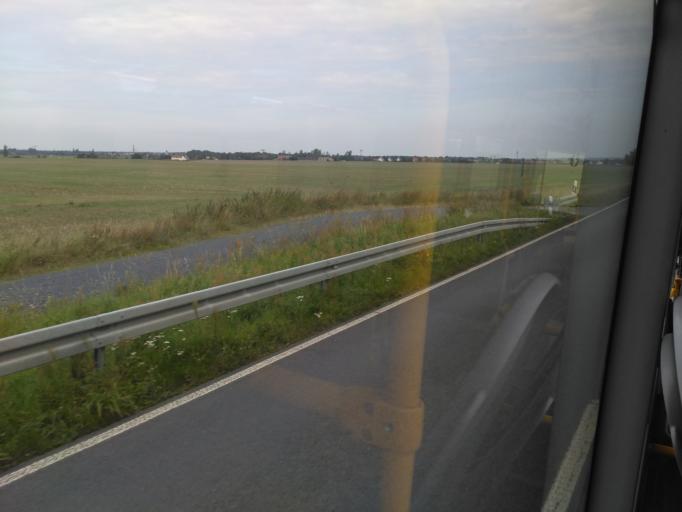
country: DE
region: Saxony
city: Priestewitz
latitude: 51.2674
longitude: 13.5161
